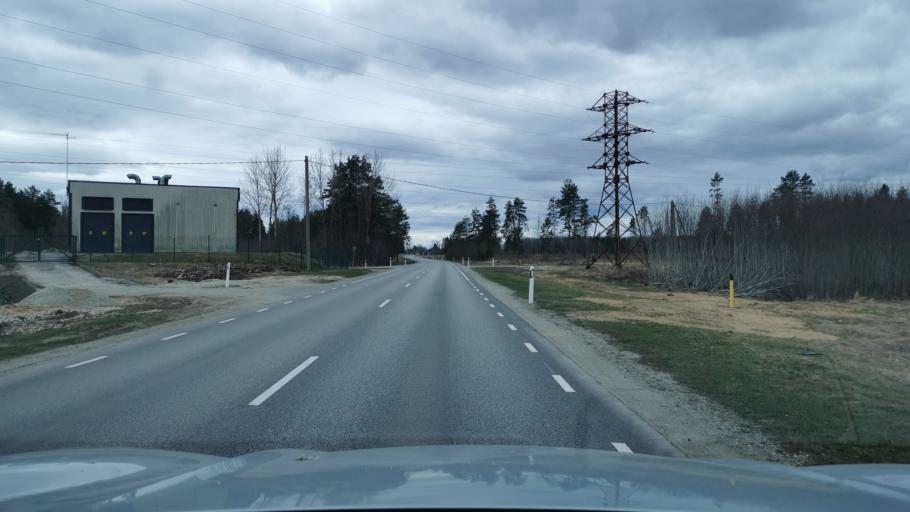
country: EE
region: Ida-Virumaa
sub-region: Puessi linn
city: Pussi
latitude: 59.3625
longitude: 27.0264
